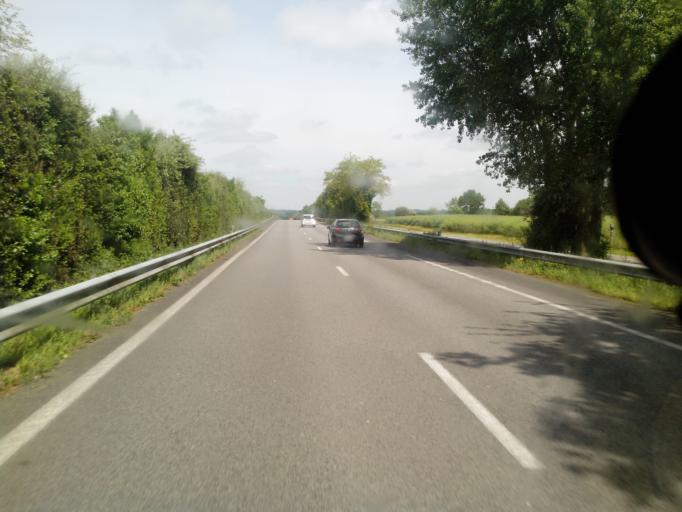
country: FR
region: Pays de la Loire
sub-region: Departement de la Loire-Atlantique
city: Jans
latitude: 47.5942
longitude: -1.6274
